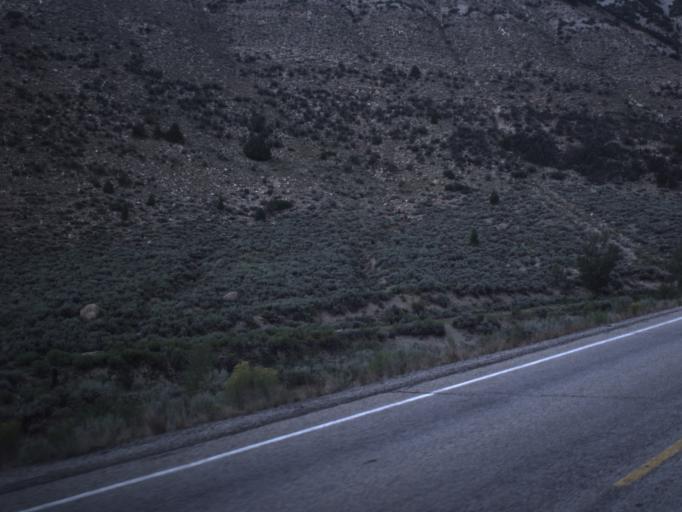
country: US
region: Utah
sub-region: Carbon County
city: Helper
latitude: 39.8418
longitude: -110.7795
